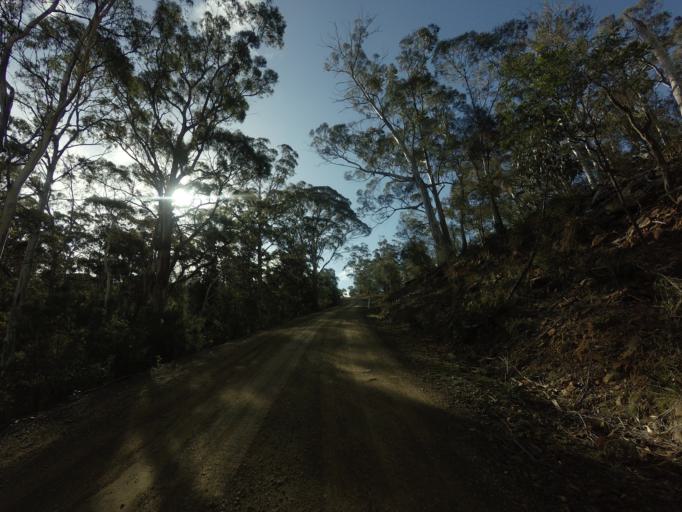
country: AU
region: Tasmania
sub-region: Sorell
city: Sorell
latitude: -42.2311
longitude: 148.0109
